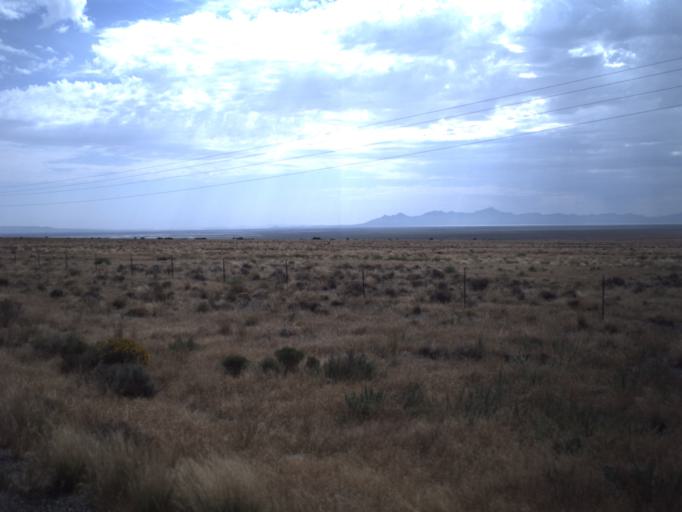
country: US
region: Utah
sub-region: Tooele County
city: Wendover
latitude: 41.4333
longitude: -113.7769
